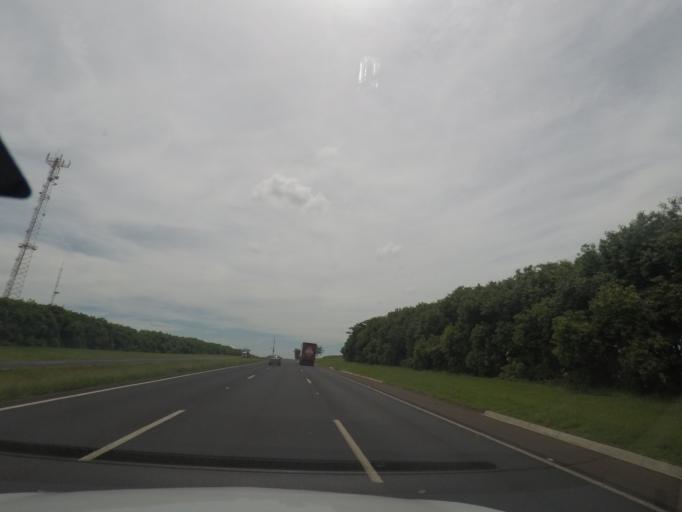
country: BR
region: Sao Paulo
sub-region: Bebedouro
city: Bebedouro
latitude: -20.9906
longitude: -48.4336
